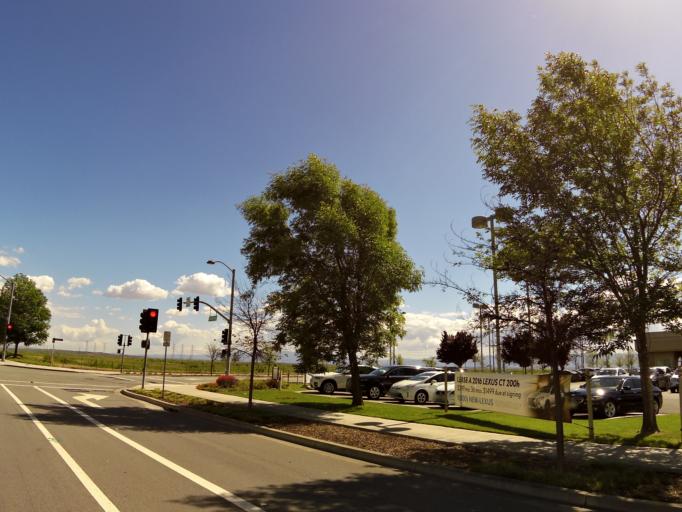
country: US
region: California
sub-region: Alameda County
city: Fremont
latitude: 37.4974
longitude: -121.9729
